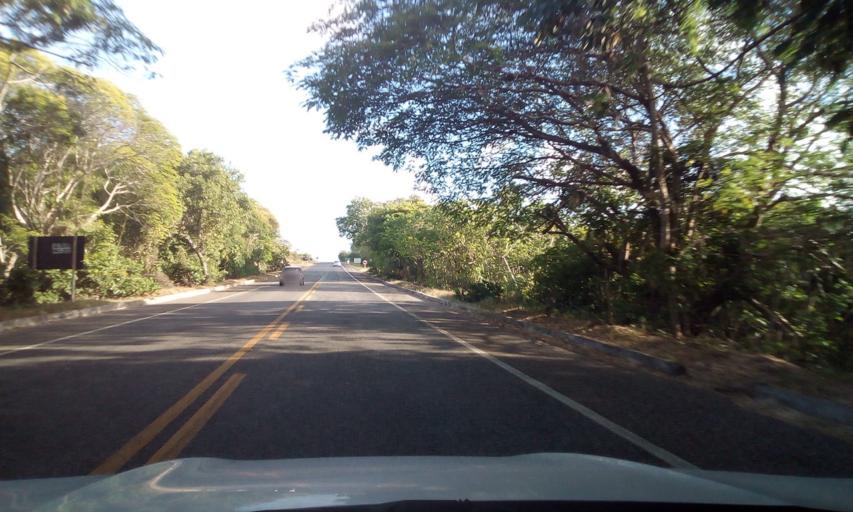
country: BR
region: Bahia
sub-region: Mata De Sao Joao
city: Mata de Sao Joao
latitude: -12.3813
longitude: -37.9120
